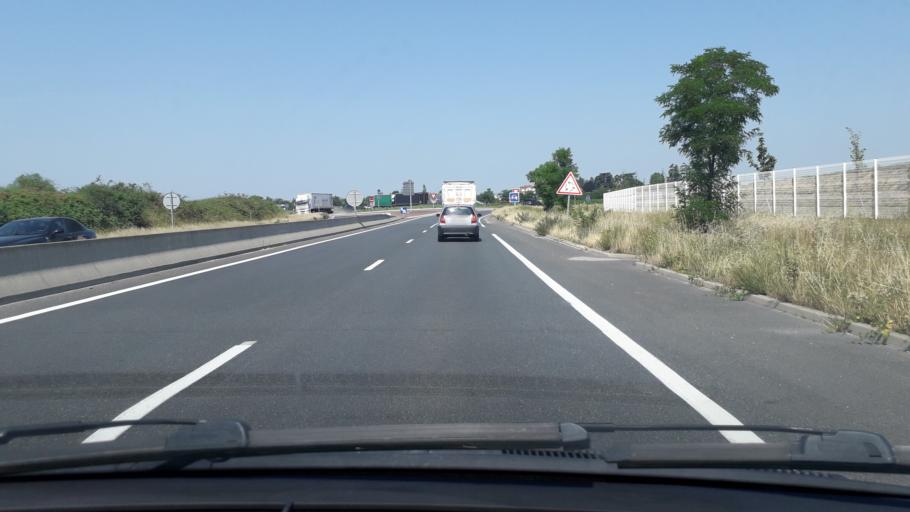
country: FR
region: Rhone-Alpes
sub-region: Departement du Rhone
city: Pusignan
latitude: 45.7663
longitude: 5.0777
